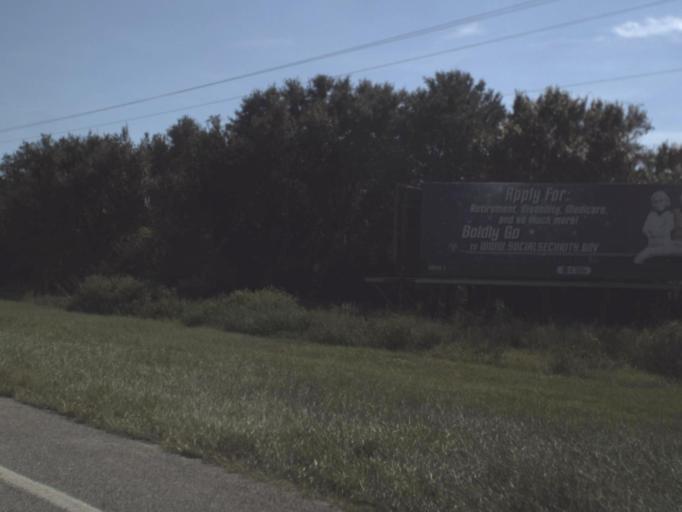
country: US
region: Florida
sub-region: Highlands County
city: Sebring
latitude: 27.3902
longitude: -81.4136
